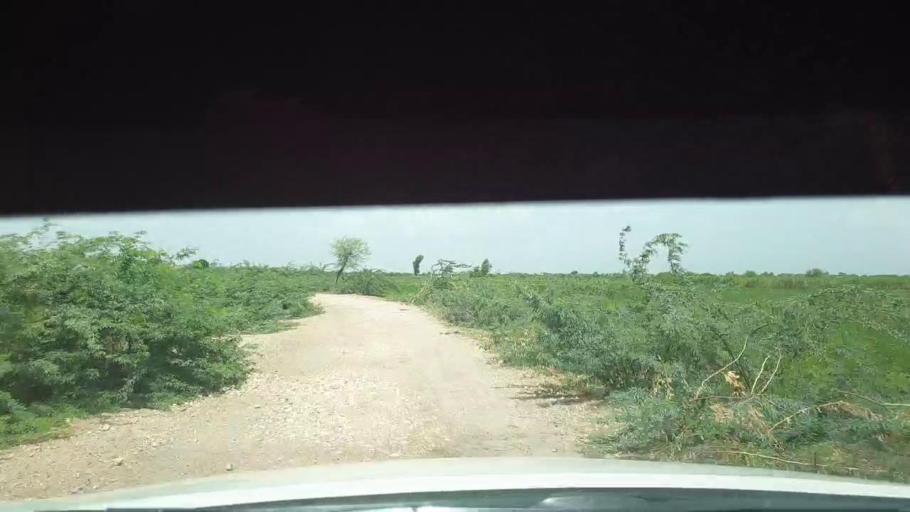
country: PK
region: Sindh
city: Kadhan
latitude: 24.5482
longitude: 68.9774
